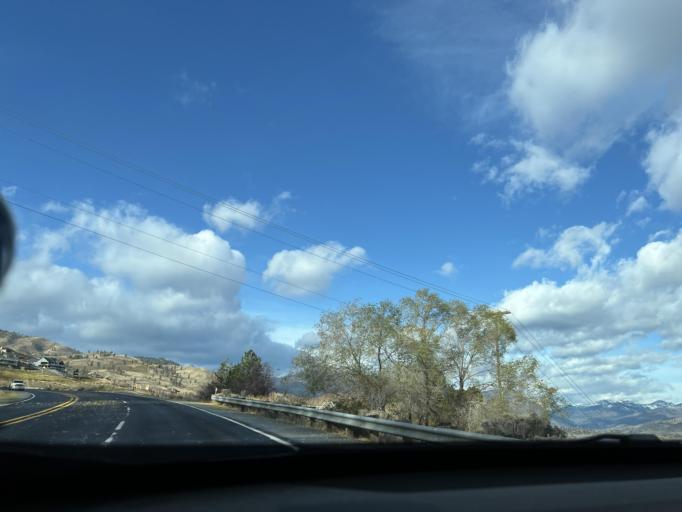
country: US
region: Washington
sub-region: Chelan County
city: Manson
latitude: 47.8415
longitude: -120.0998
